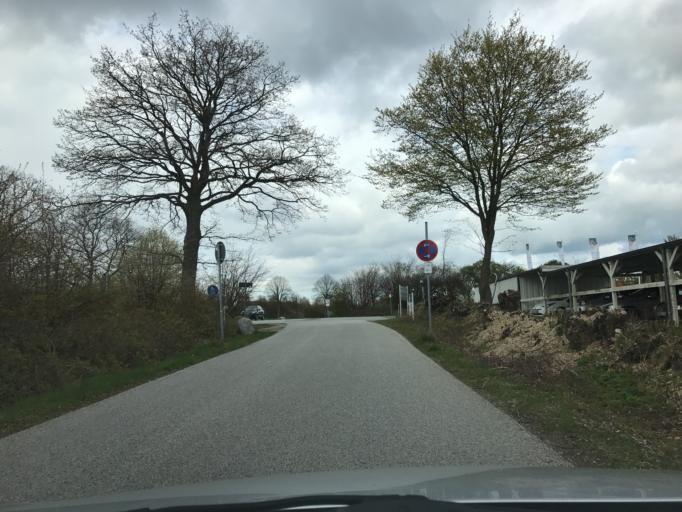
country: DE
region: Schleswig-Holstein
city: Neustadt in Holstein
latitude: 54.0905
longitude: 10.8316
